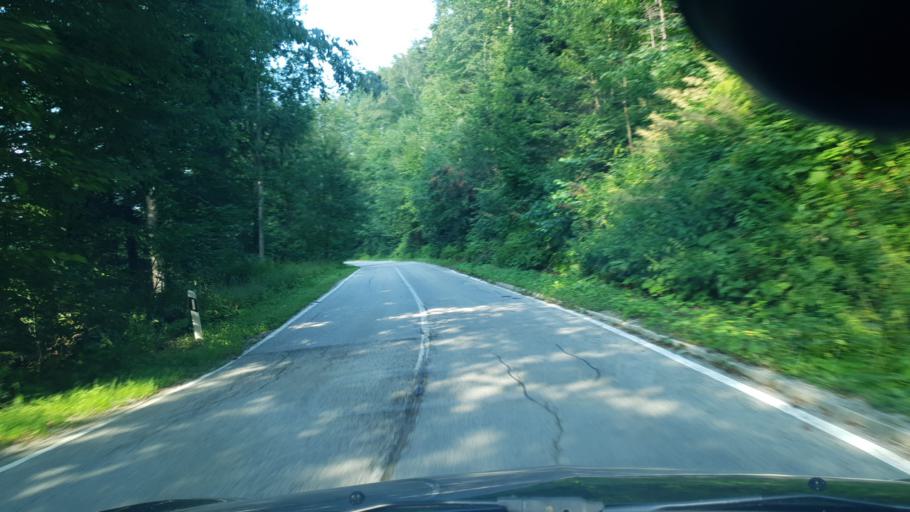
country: HR
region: Grad Zagreb
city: Kasina
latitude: 45.9178
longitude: 15.9807
